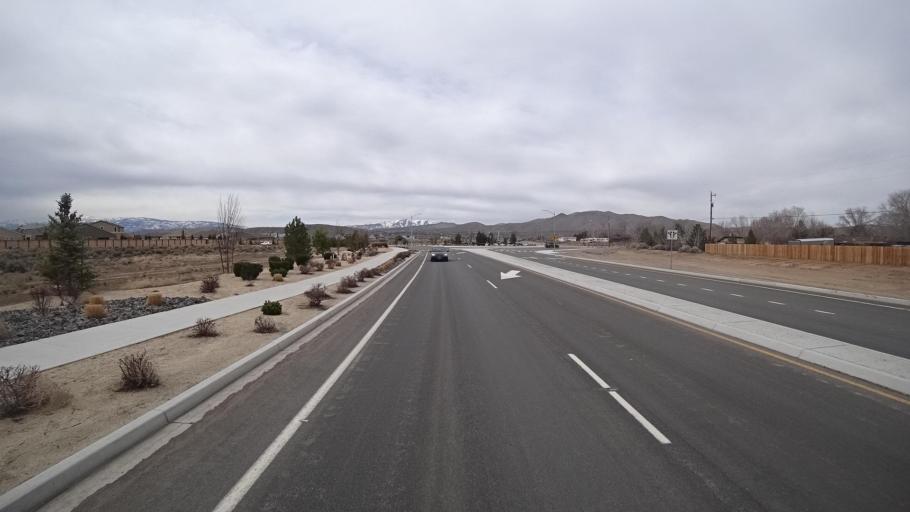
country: US
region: Nevada
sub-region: Washoe County
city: Spanish Springs
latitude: 39.6361
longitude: -119.6982
